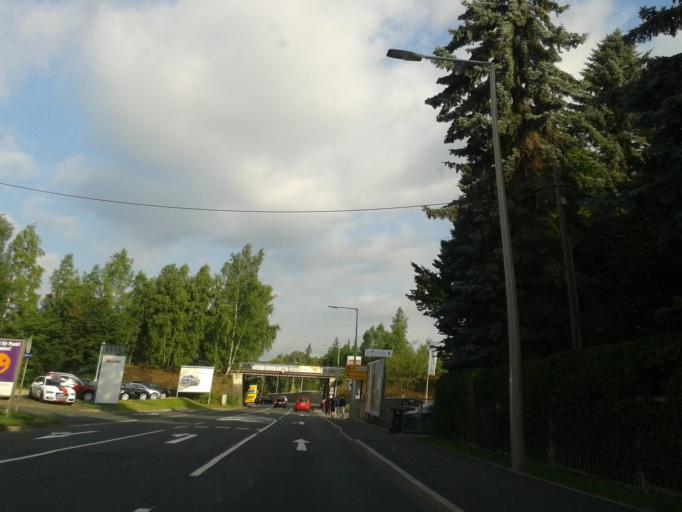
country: DE
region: Saxony
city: Freiberg
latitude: 50.9157
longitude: 13.3589
